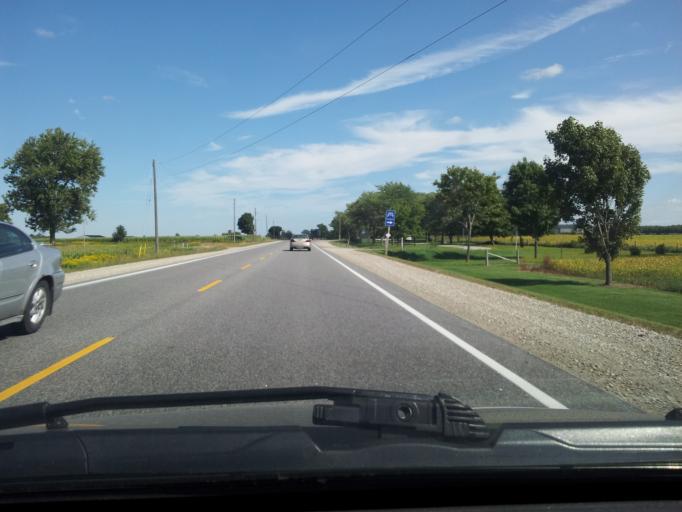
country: CA
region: Ontario
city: Stratford
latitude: 43.3690
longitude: -80.7743
